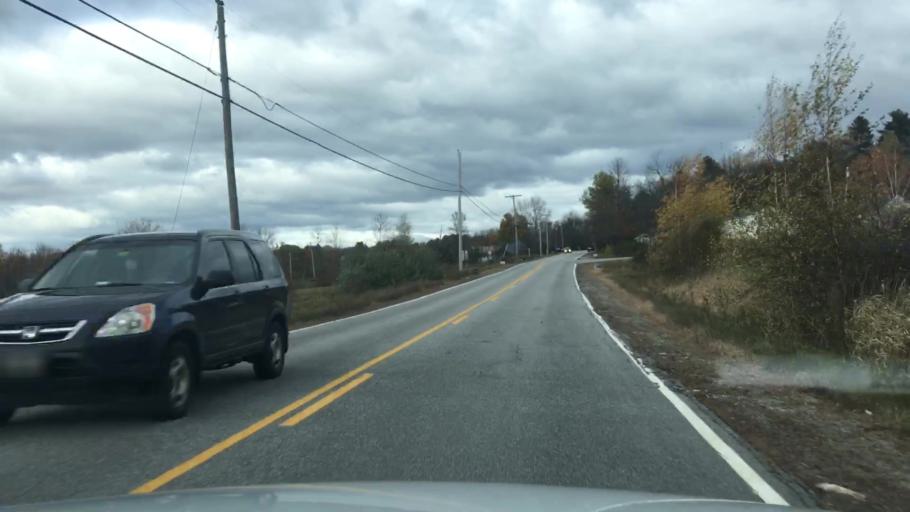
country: US
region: Maine
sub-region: Androscoggin County
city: Sabattus
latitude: 44.1623
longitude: -70.0775
